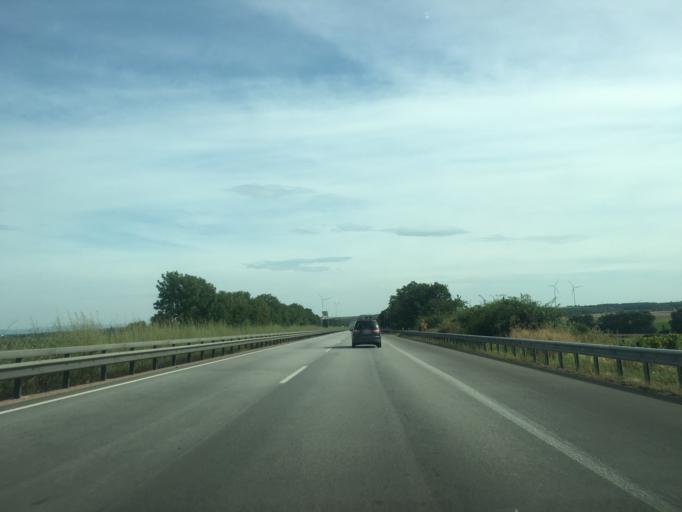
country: DE
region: Rheinland-Pfalz
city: Gundheim
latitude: 49.6806
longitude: 8.2518
